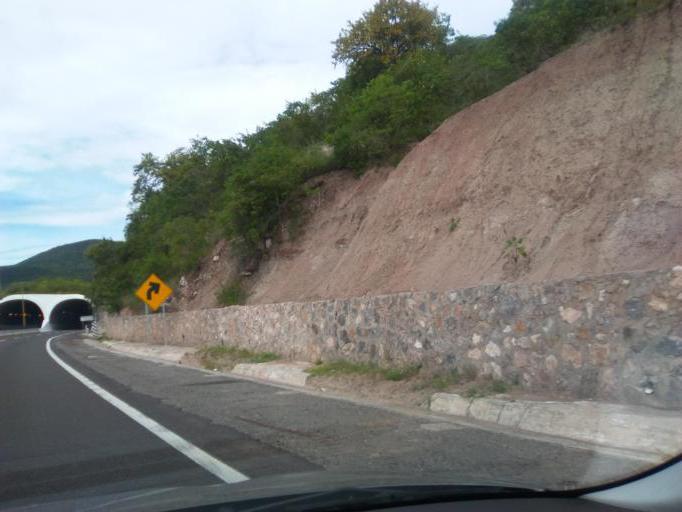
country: MX
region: Guerrero
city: Zumpango del Rio
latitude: 17.6700
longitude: -99.4960
